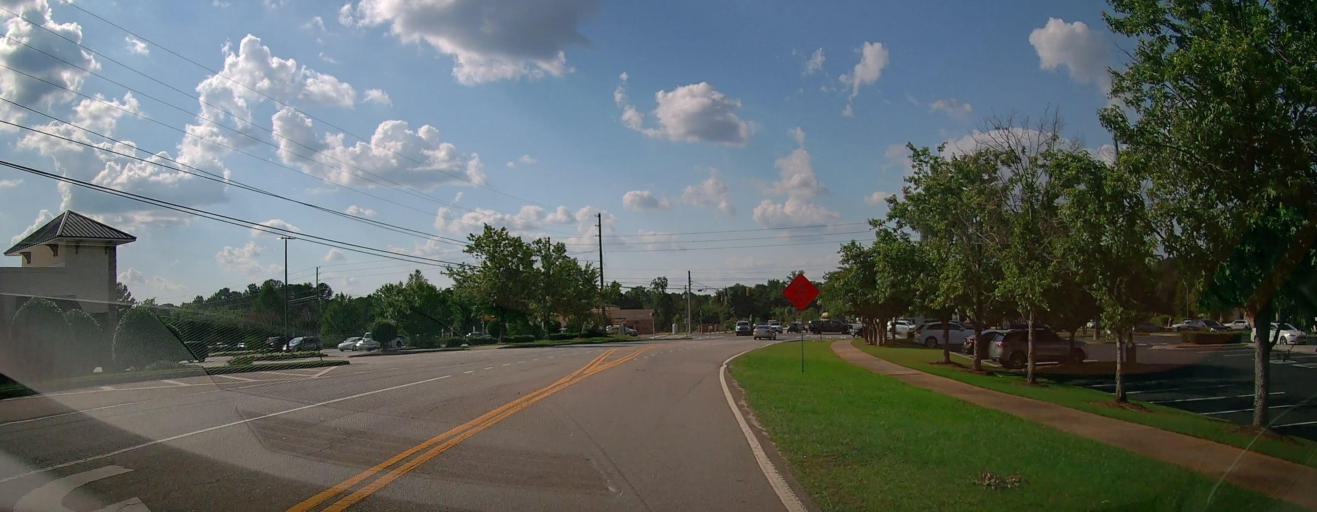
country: US
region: Georgia
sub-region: Henry County
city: Stockbridge
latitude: 33.4634
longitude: -84.2319
